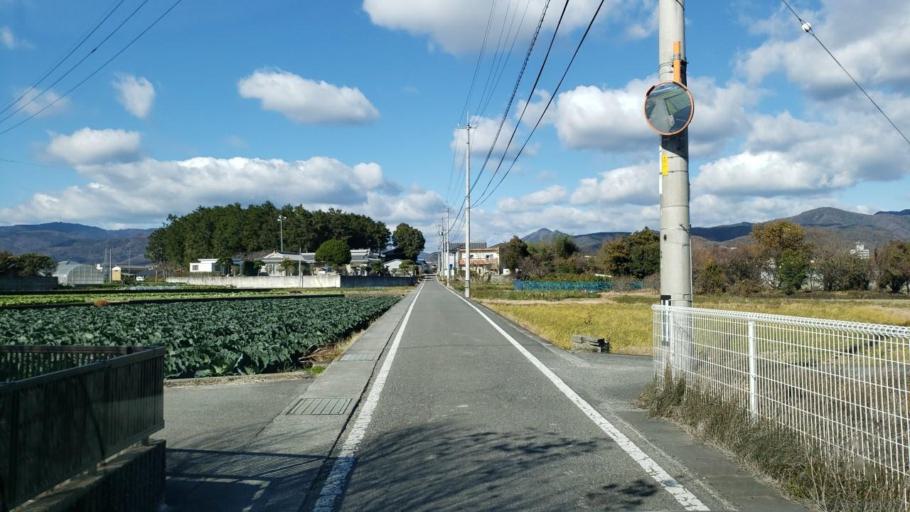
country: JP
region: Tokushima
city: Kamojimacho-jogejima
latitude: 34.0814
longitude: 134.2941
